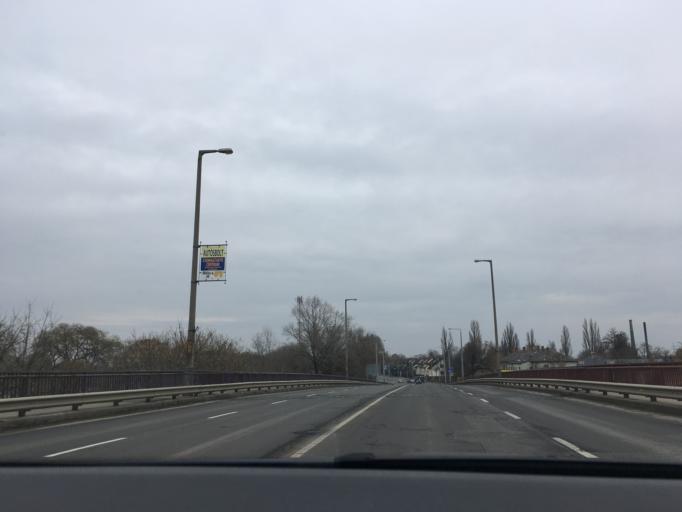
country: HU
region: Hajdu-Bihar
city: Debrecen
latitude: 47.5292
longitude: 21.6459
